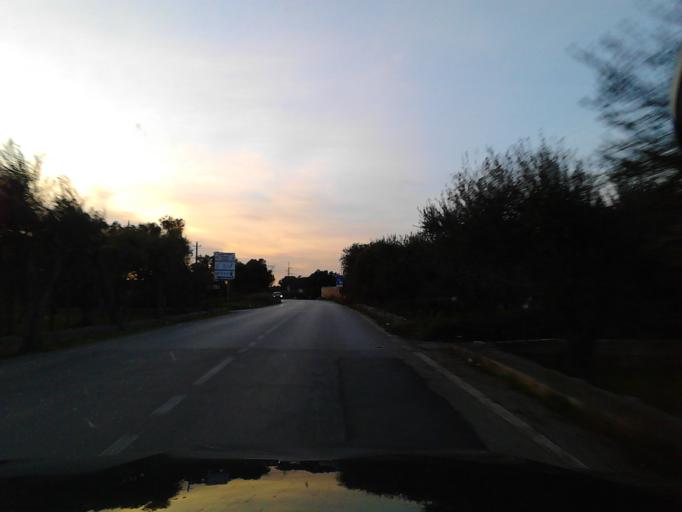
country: IT
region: Apulia
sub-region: Provincia di Bari
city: Lamie
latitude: 41.0394
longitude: 16.8670
